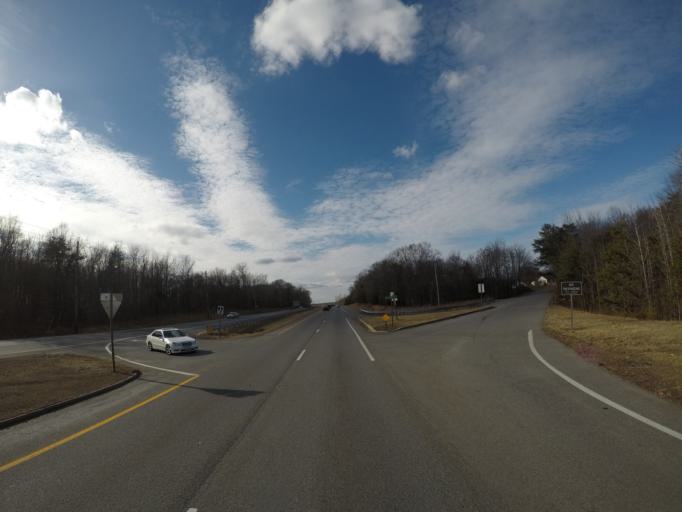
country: US
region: Maryland
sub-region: Charles County
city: Waldorf
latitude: 38.6507
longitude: -76.9632
